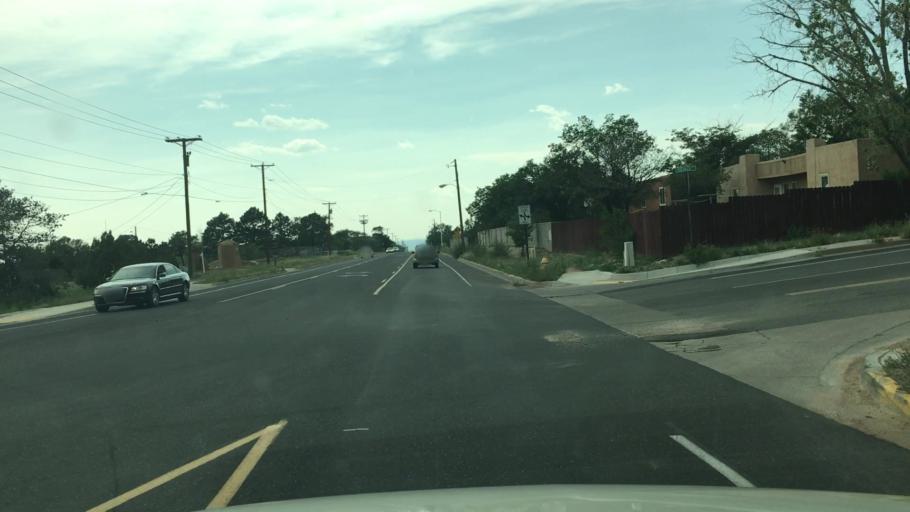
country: US
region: New Mexico
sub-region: Santa Fe County
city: Santa Fe
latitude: 35.6522
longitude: -105.9583
